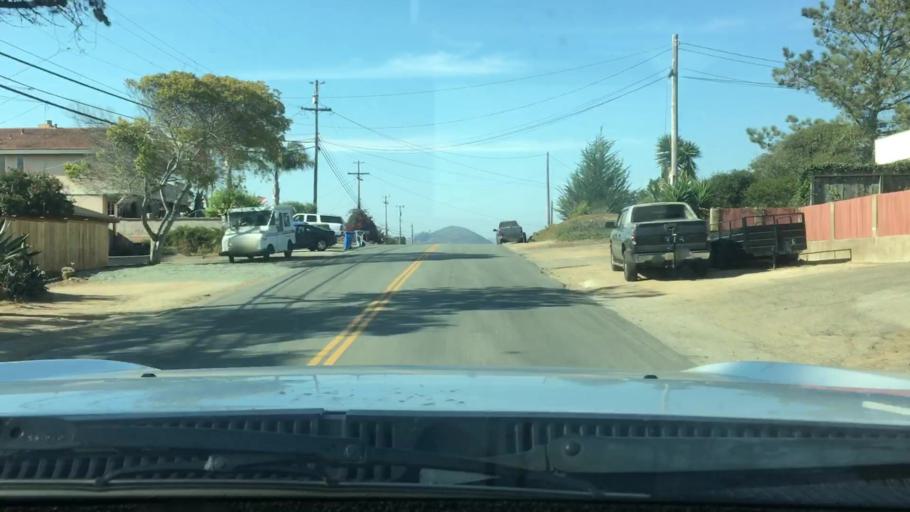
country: US
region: California
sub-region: San Luis Obispo County
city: Los Osos
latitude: 35.3214
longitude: -120.8311
